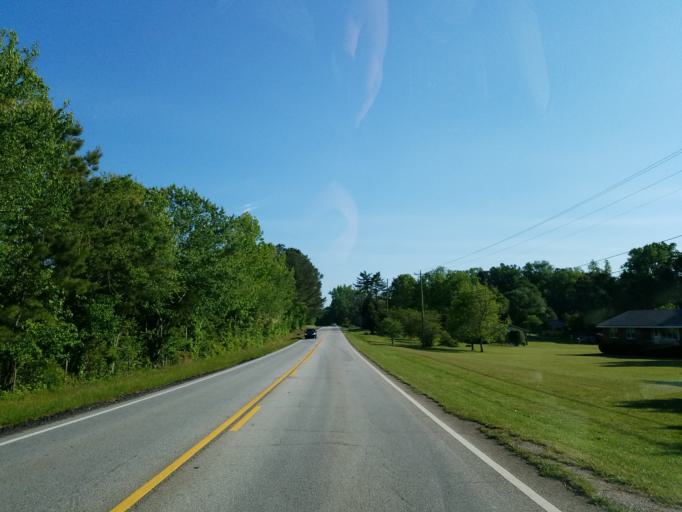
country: US
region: Georgia
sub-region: Carroll County
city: Temple
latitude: 33.8357
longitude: -84.9802
